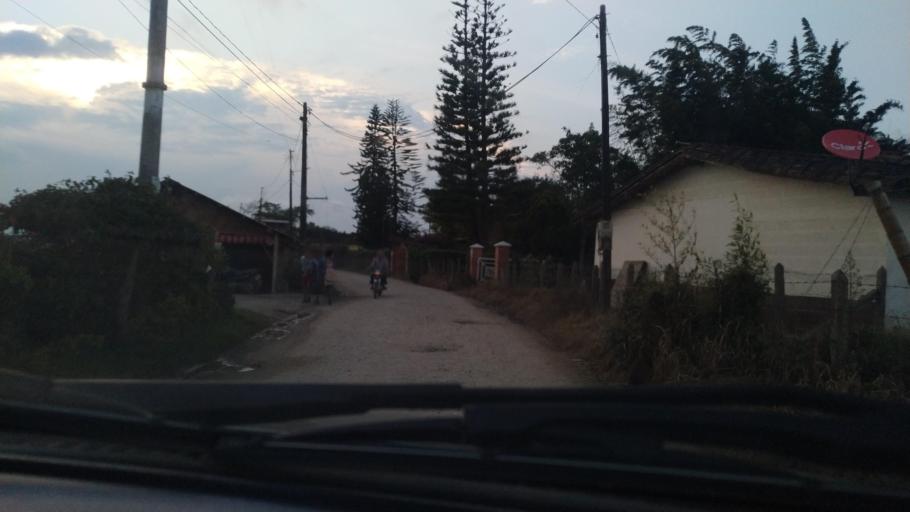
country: CO
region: Antioquia
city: Marinilla
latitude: 6.1938
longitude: -75.2839
